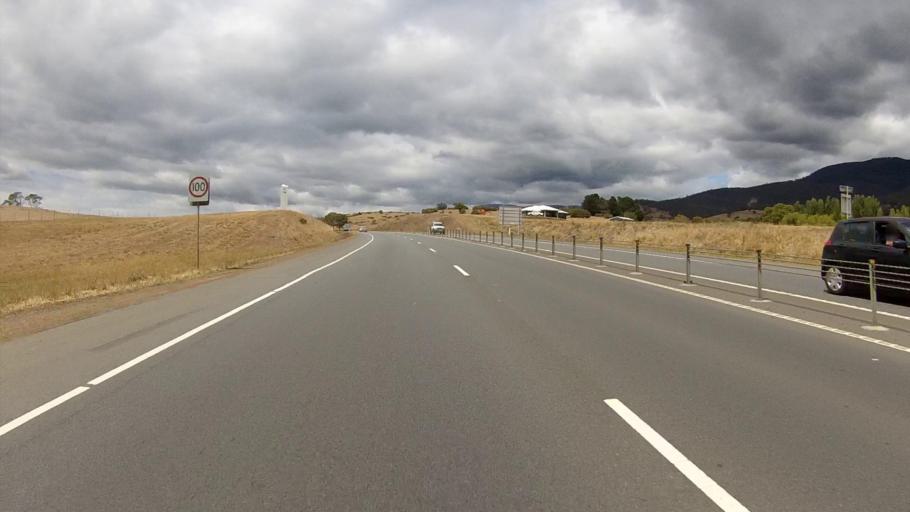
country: AU
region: Tasmania
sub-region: Glenorchy
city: Granton
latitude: -42.7562
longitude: 147.2299
